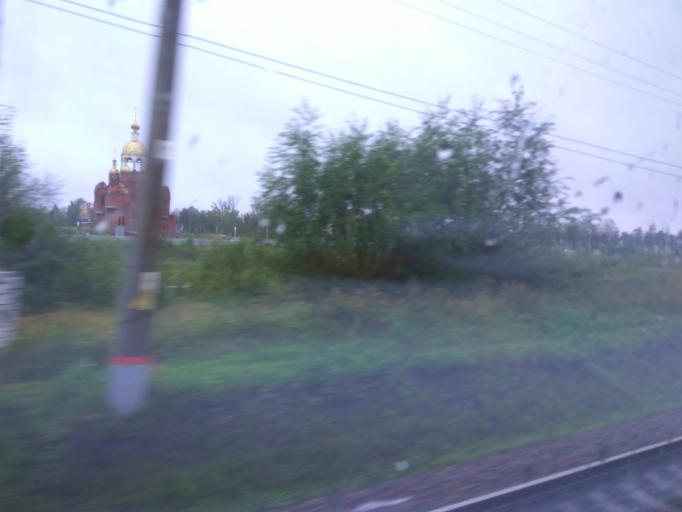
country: RU
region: Moskovskaya
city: Stupino
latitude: 54.9025
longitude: 38.0852
